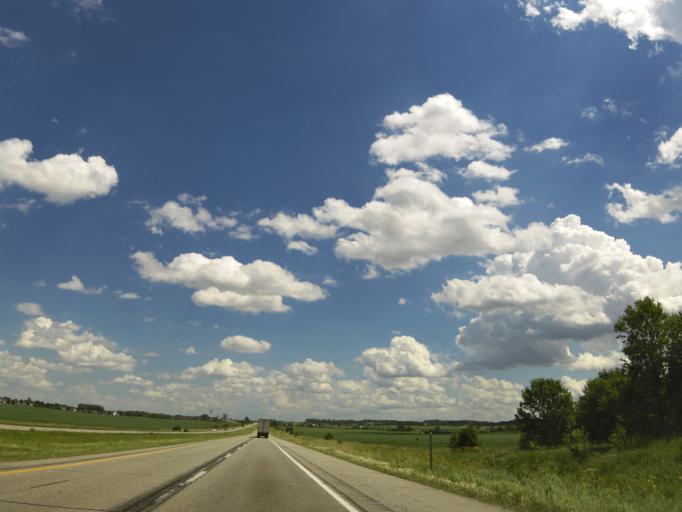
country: US
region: Iowa
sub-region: Linn County
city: Center Point
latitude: 42.1838
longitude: -91.7985
